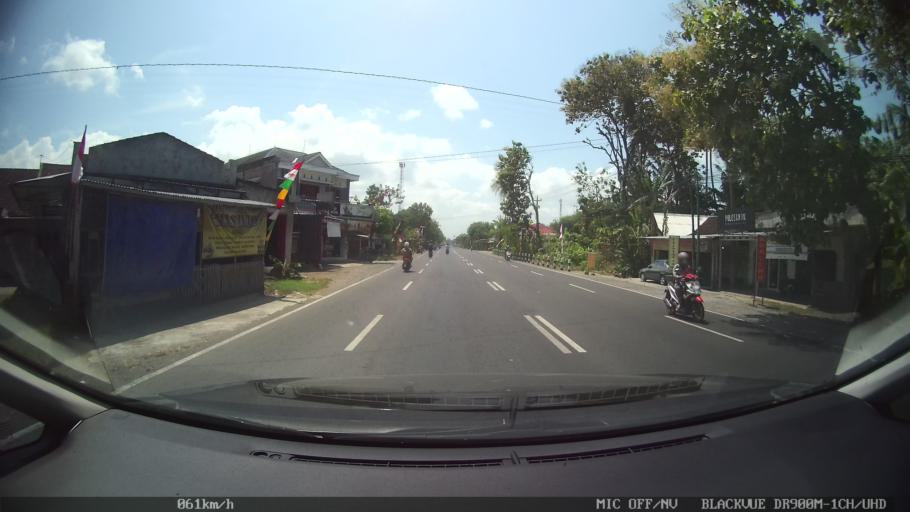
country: ID
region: Daerah Istimewa Yogyakarta
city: Srandakan
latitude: -7.9366
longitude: 110.2587
